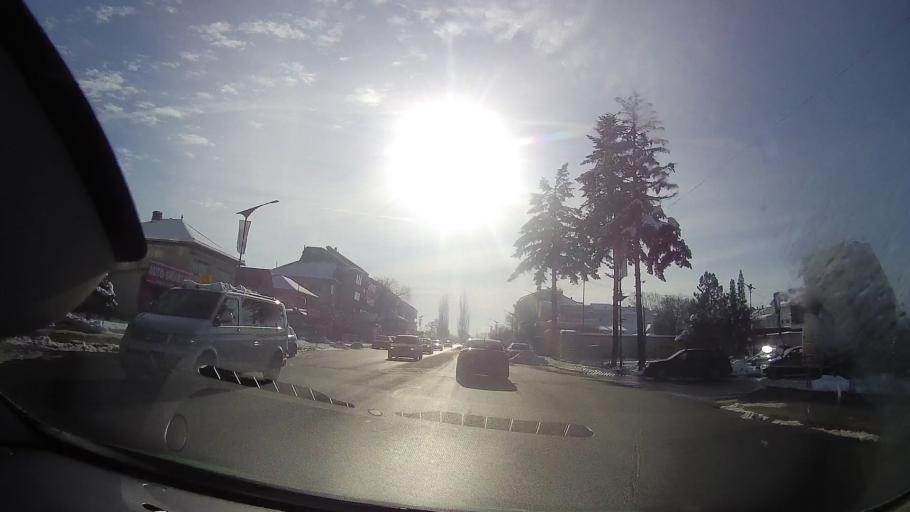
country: RO
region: Neamt
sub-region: Oras Targu Neamt
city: Humulesti
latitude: 47.2035
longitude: 26.3583
